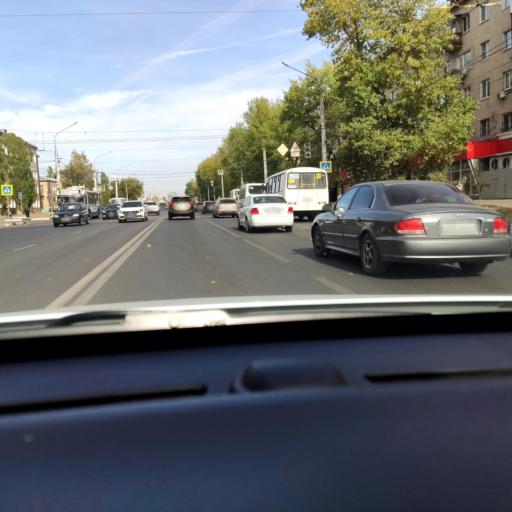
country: RU
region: Voronezj
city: Voronezh
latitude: 51.6550
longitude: 39.2436
